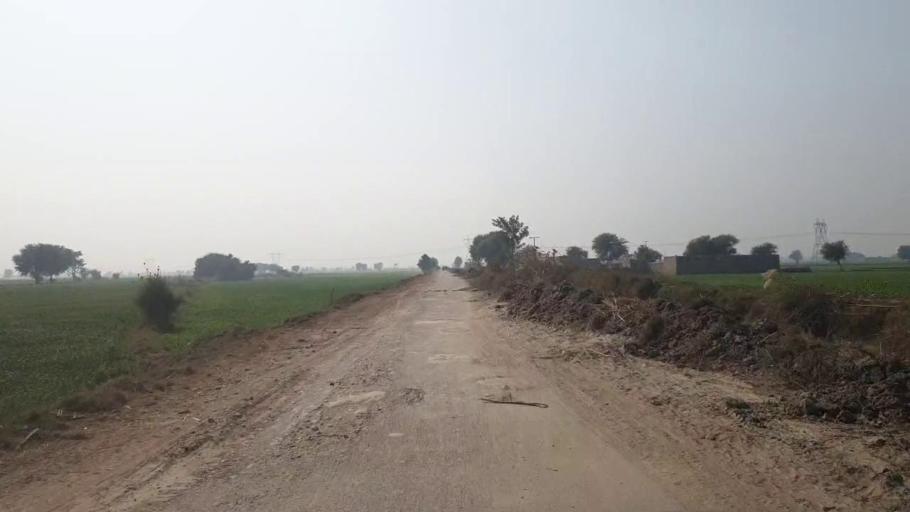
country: PK
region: Sindh
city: Hala
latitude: 25.9456
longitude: 68.4510
